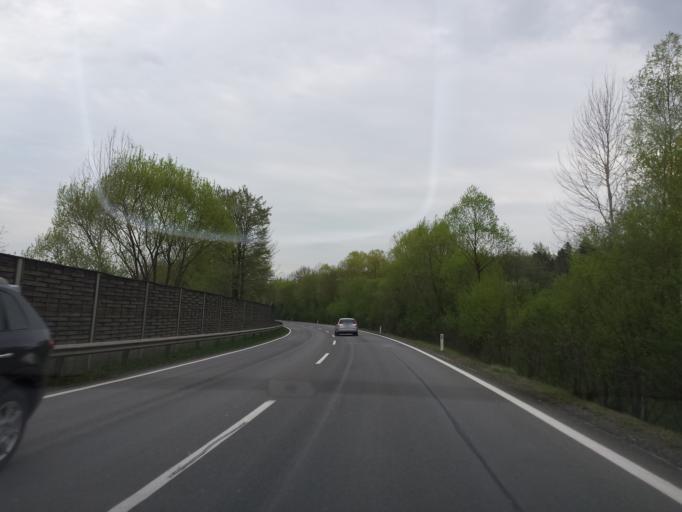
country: AT
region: Styria
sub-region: Politischer Bezirk Hartberg-Fuerstenfeld
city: Altenmarkt bei Fuerstenfeld
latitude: 47.0618
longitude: 16.0490
